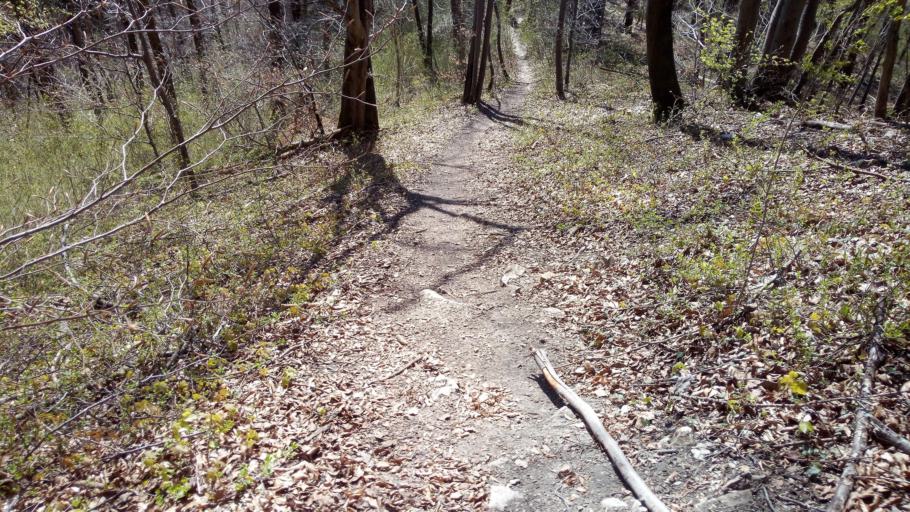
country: DE
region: Baden-Wuerttemberg
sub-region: Regierungsbezirk Stuttgart
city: Donzdorf
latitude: 48.7126
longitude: 9.8423
